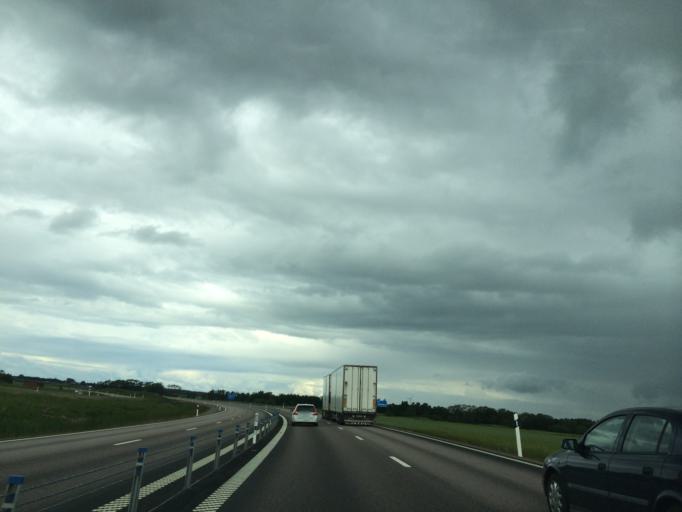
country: SE
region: OEstergoetland
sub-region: Mjolby Kommun
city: Mjolby
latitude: 58.3949
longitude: 15.1055
